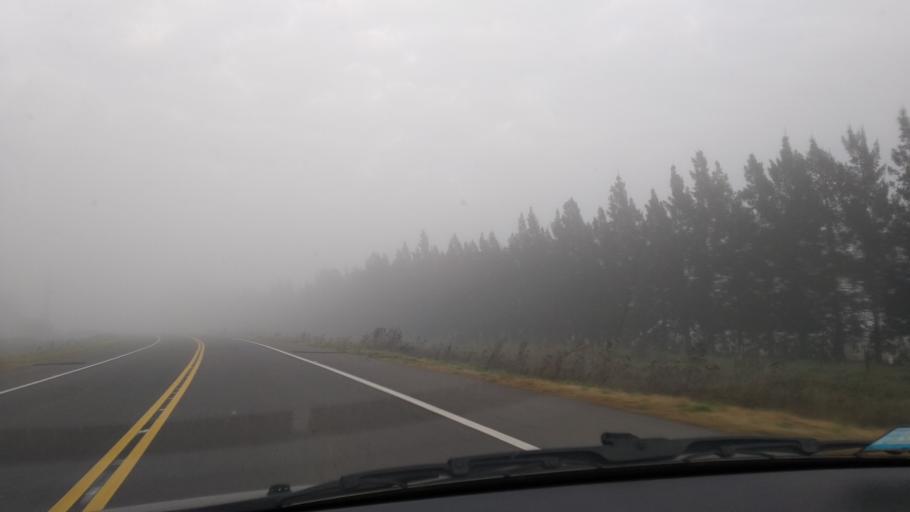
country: AR
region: Buenos Aires
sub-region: Partido de Brandsen
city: Brandsen
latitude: -35.1974
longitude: -58.3883
